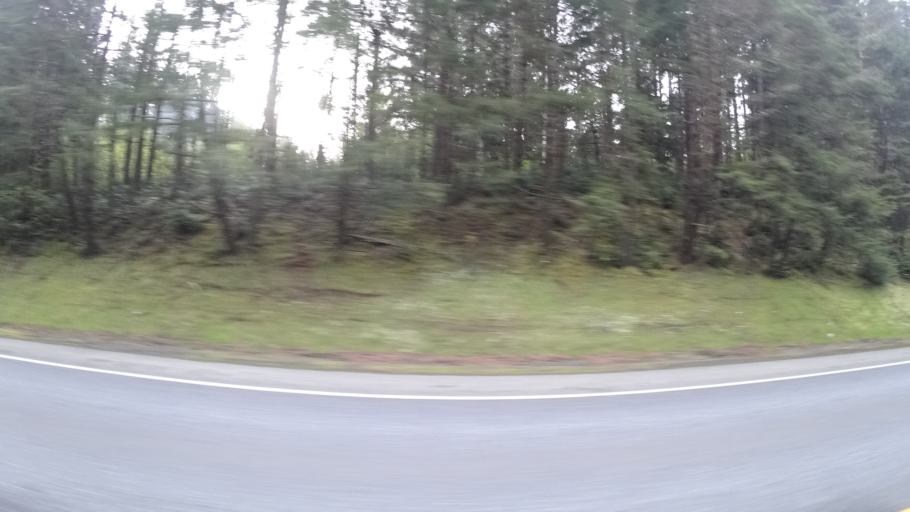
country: US
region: Oregon
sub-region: Coos County
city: Lakeside
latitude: 43.5575
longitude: -124.2076
